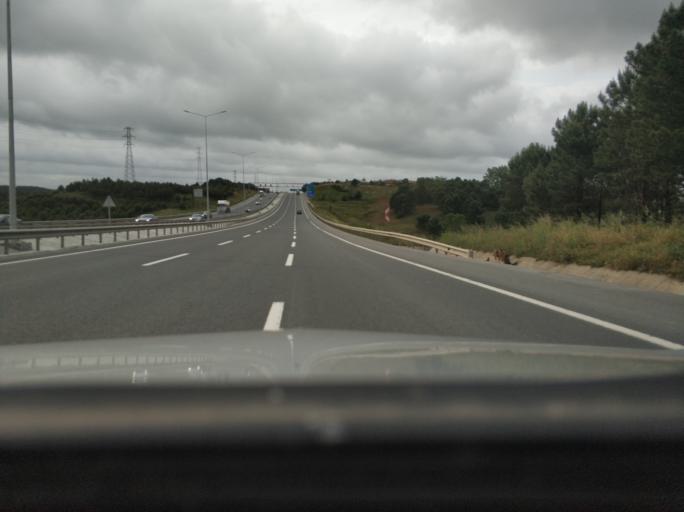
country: TR
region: Istanbul
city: Kemerburgaz
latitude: 41.1533
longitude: 28.9000
